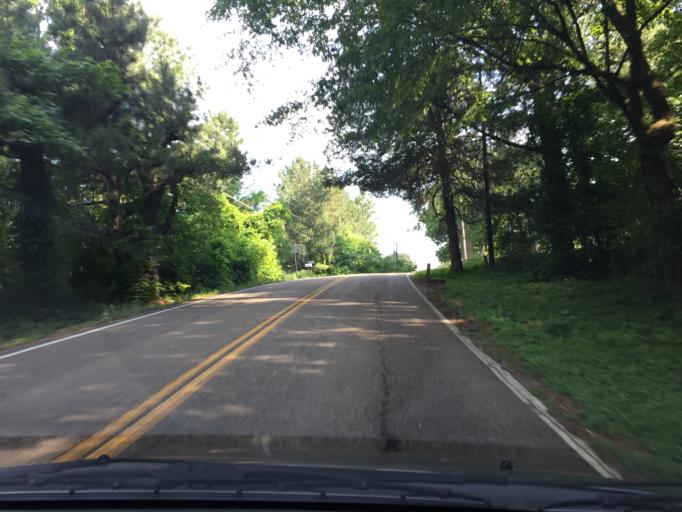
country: US
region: Tennessee
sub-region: Hamilton County
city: Apison
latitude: 35.0318
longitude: -85.0252
